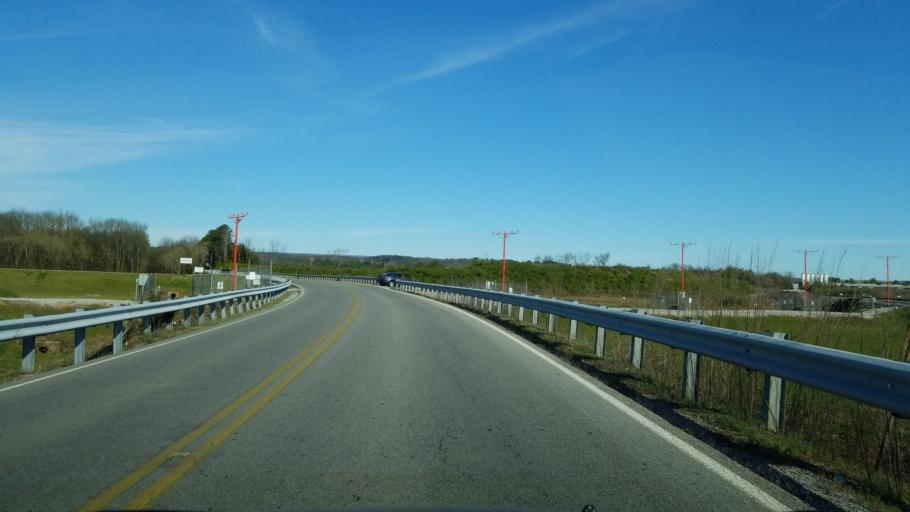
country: US
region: Tennessee
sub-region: Hamilton County
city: East Chattanooga
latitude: 35.0452
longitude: -85.1985
